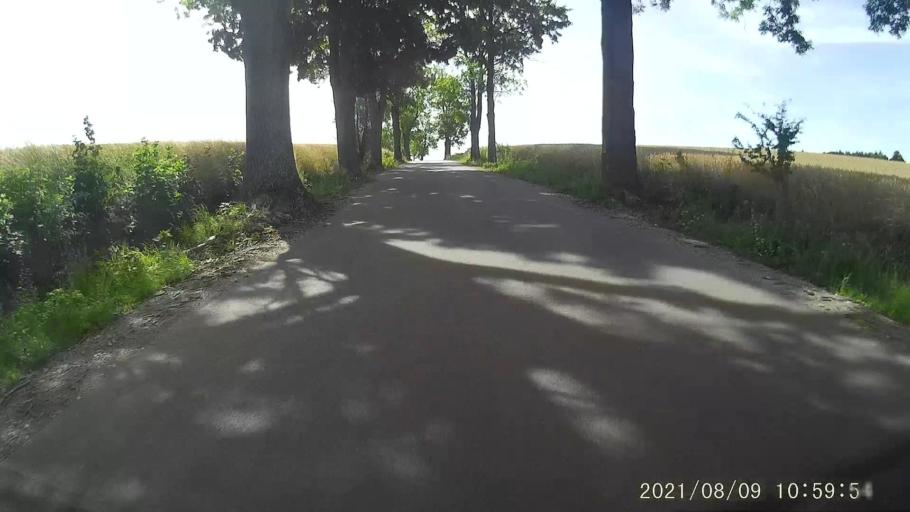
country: PL
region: Lower Silesian Voivodeship
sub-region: Powiat klodzki
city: Polanica-Zdroj
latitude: 50.4518
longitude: 16.5468
